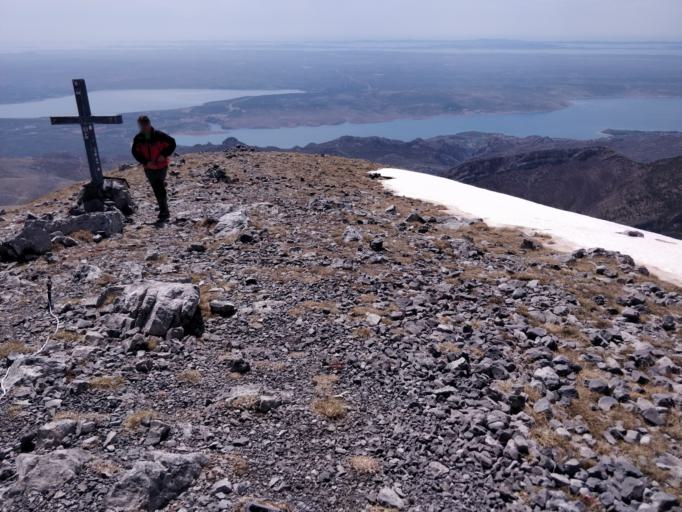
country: HR
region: Zadarska
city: Starigrad
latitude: 44.3285
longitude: 15.5695
